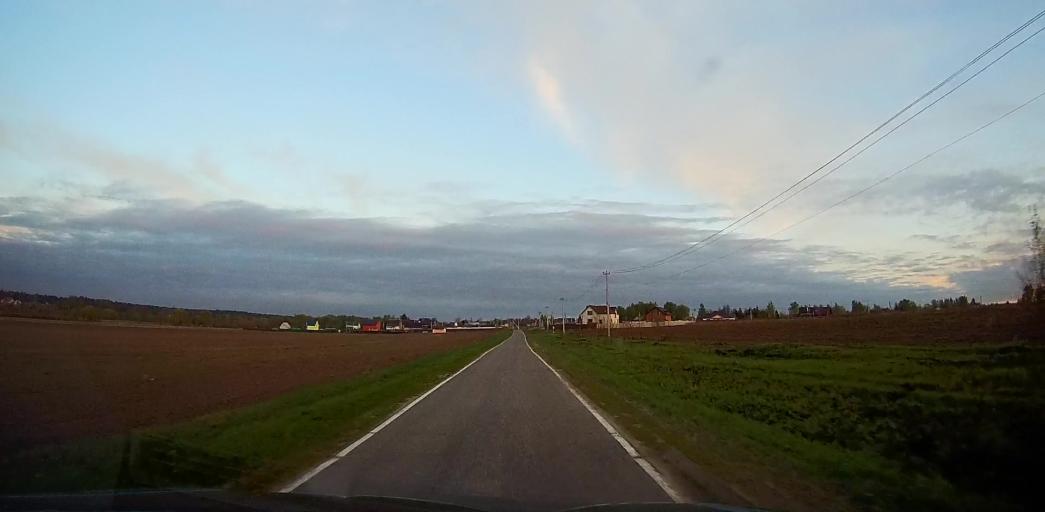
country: RU
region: Moskovskaya
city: Peski
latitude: 55.2168
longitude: 38.7385
